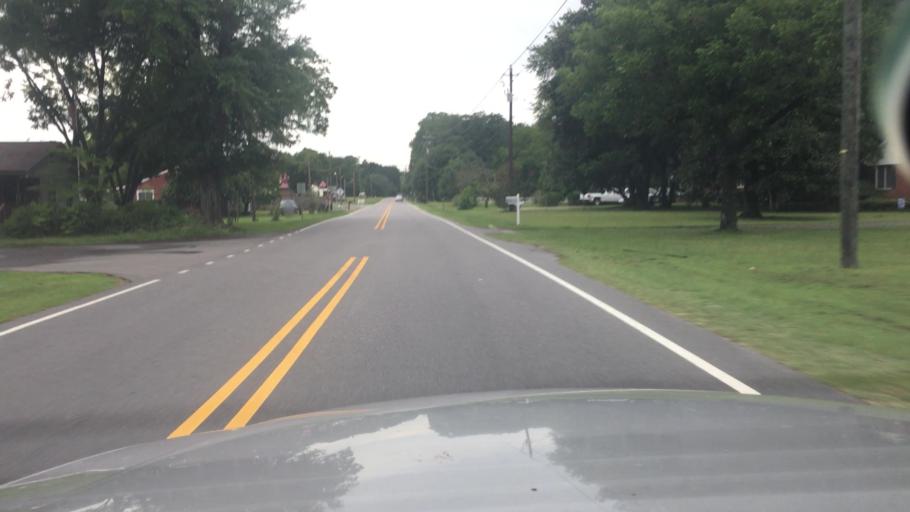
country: US
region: North Carolina
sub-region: Cumberland County
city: Hope Mills
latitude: 34.9668
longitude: -78.9265
